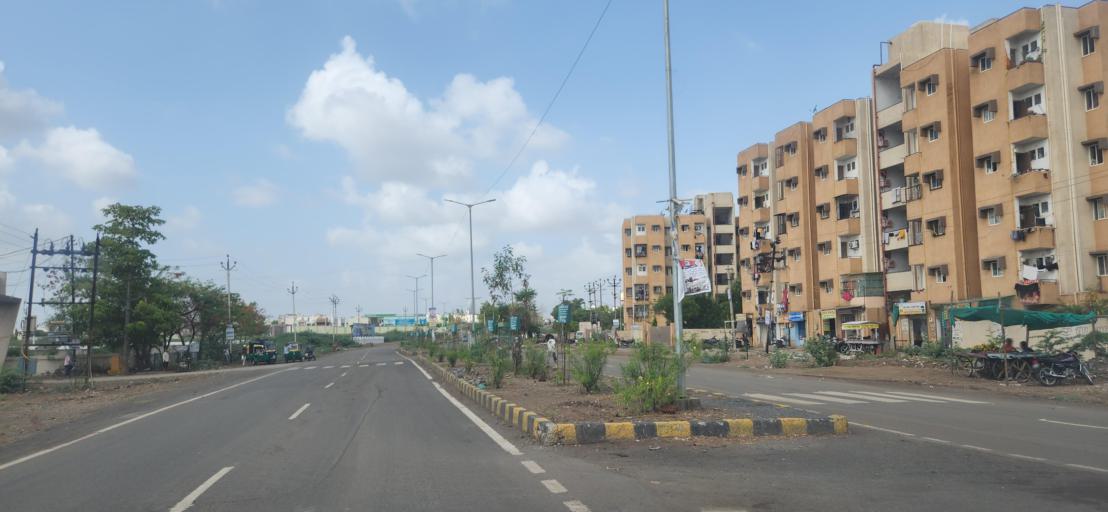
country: IN
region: Gujarat
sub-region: Bhavnagar
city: Bhavnagar
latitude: 21.7578
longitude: 72.1734
